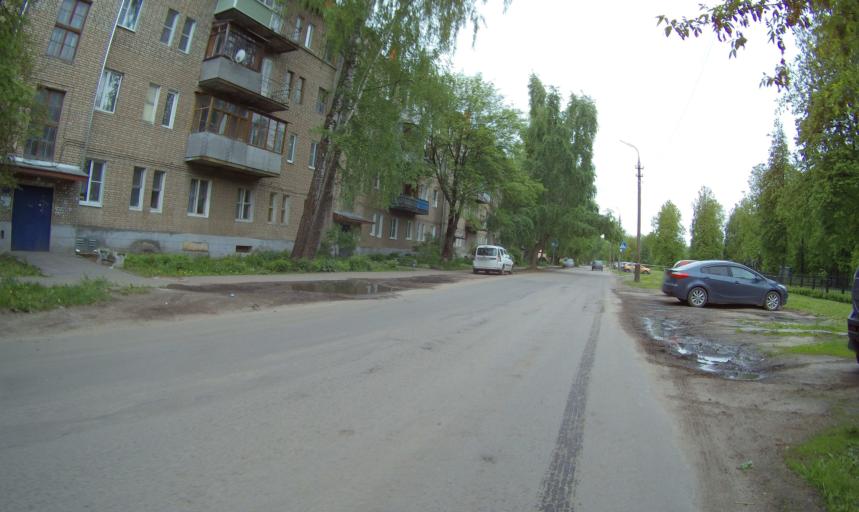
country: RU
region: Moskovskaya
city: Kolomna
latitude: 55.0779
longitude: 38.8050
